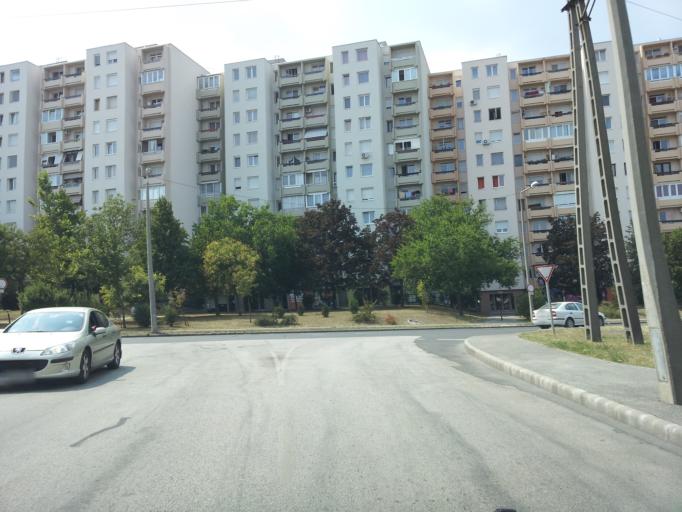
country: HU
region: Veszprem
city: Veszprem
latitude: 47.1096
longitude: 17.9172
